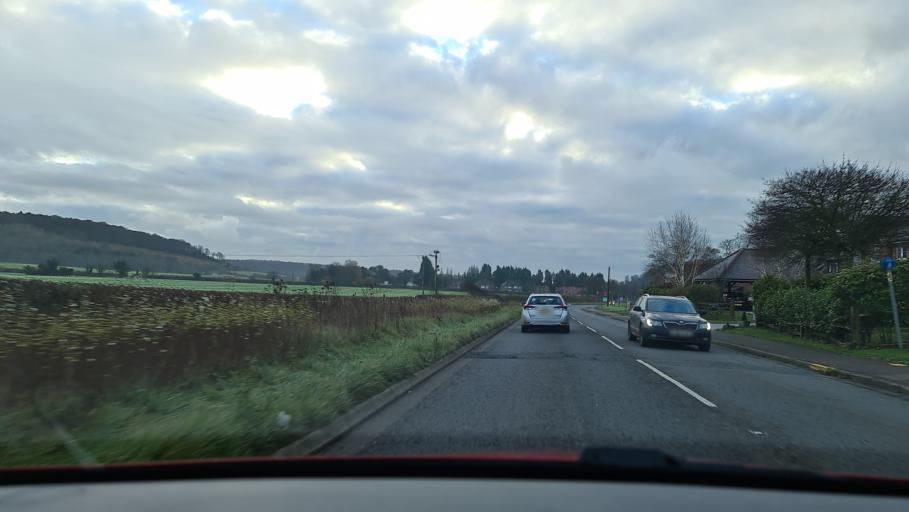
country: GB
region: England
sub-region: Buckinghamshire
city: Princes Risborough
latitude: 51.6792
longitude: -0.8266
